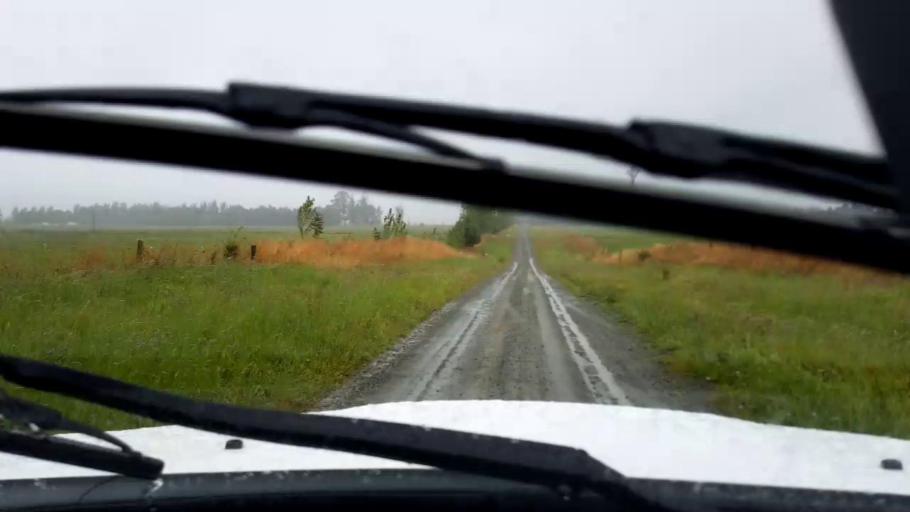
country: NZ
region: Canterbury
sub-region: Timaru District
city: Pleasant Point
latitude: -44.1982
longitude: 171.0908
